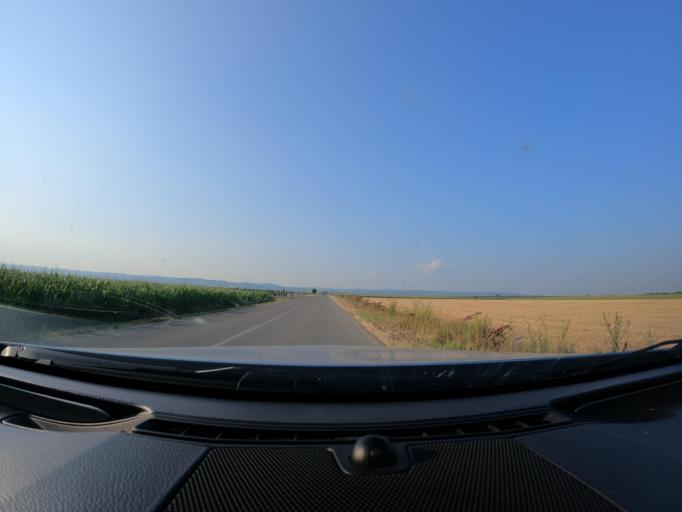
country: RS
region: Autonomna Pokrajina Vojvodina
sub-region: Sremski Okrug
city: Ruma
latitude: 45.0523
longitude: 19.7654
